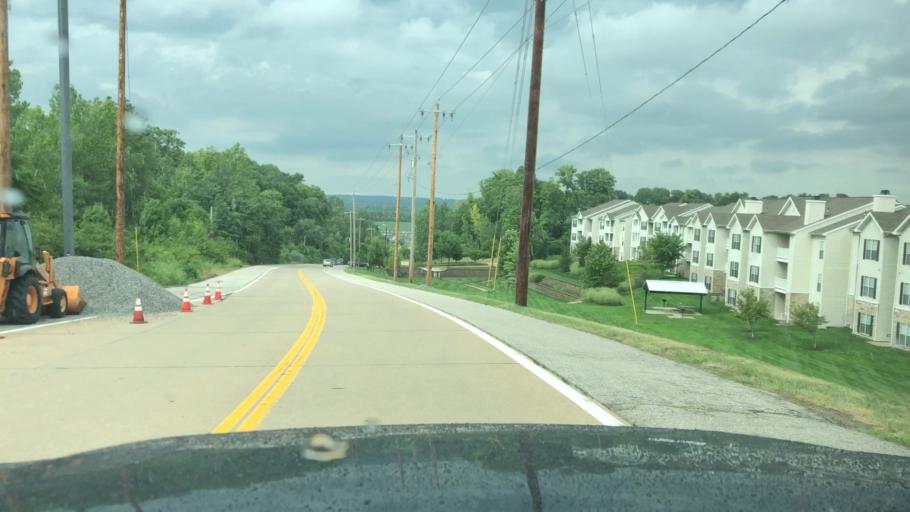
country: US
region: Missouri
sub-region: Saint Charles County
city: Saint Peters
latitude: 38.7993
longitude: -90.5803
